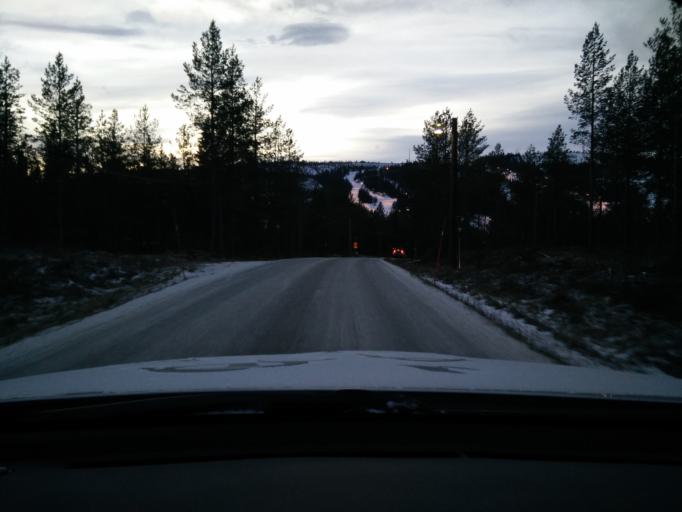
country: SE
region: Jaemtland
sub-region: Bergs Kommun
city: Hoverberg
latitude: 62.5055
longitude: 14.1969
